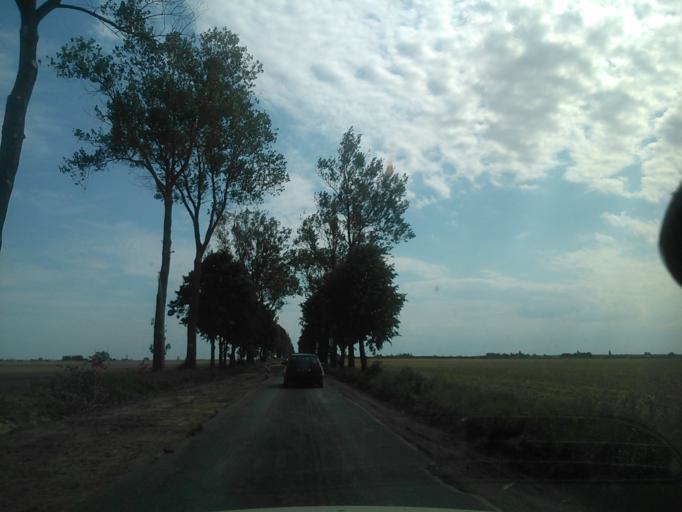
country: PL
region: Warmian-Masurian Voivodeship
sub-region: Powiat dzialdowski
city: Ilowo -Osada
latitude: 53.1866
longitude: 20.2834
